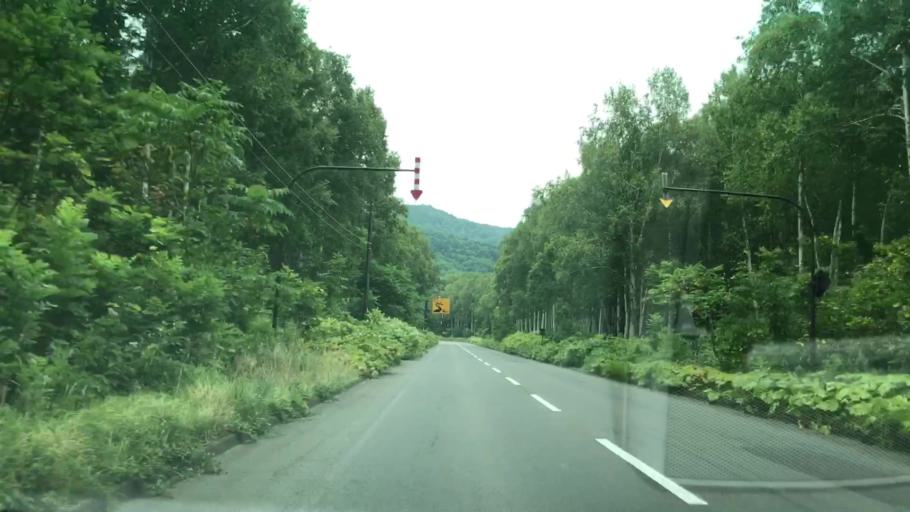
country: JP
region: Hokkaido
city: Yoichi
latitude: 43.0083
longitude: 140.8739
